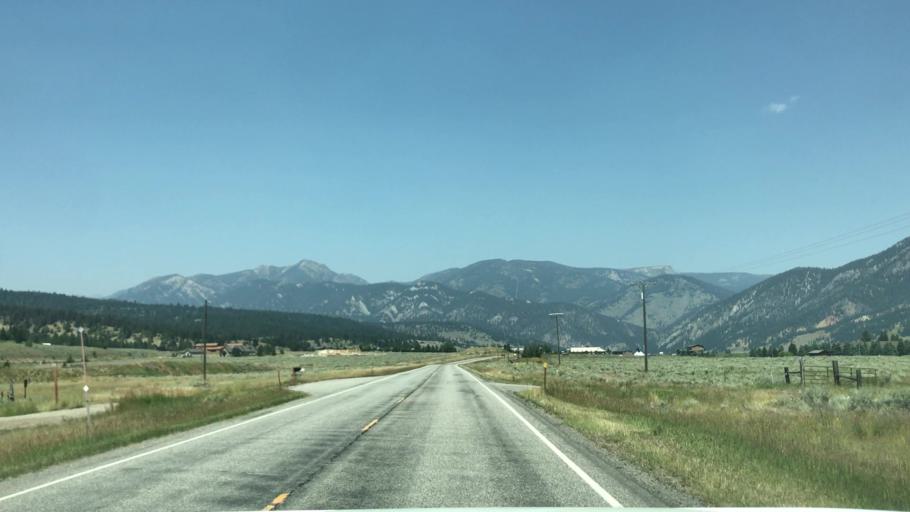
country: US
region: Montana
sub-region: Gallatin County
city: Big Sky
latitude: 45.2170
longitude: -111.2493
